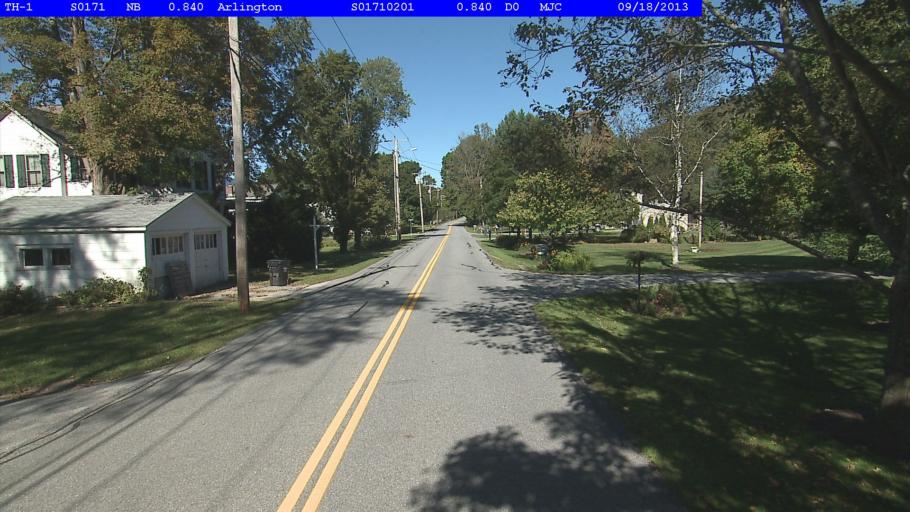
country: US
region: Vermont
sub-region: Bennington County
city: Arlington
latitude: 43.0651
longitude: -73.1412
